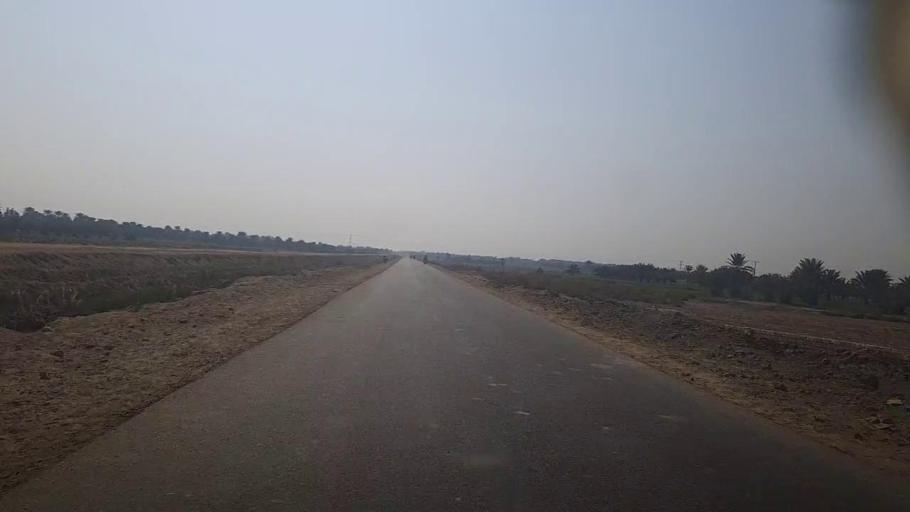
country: PK
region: Sindh
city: Khairpur
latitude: 27.4762
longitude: 68.8242
